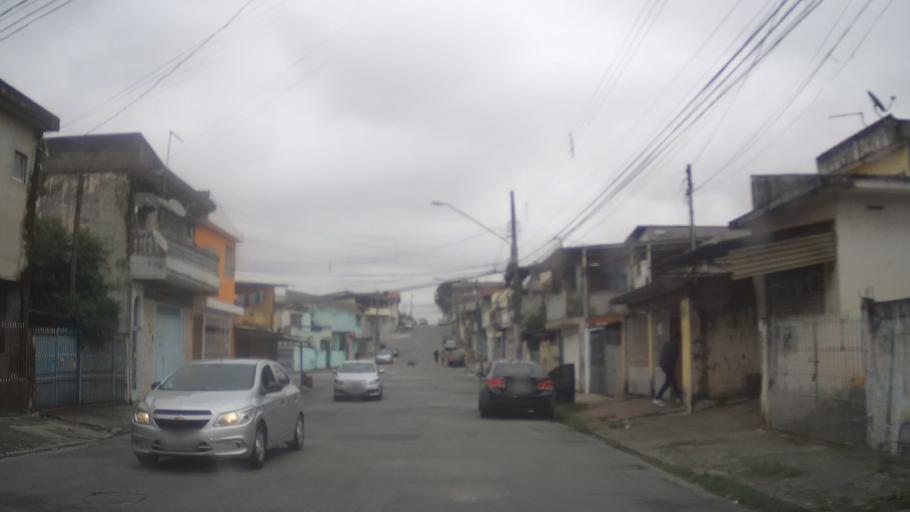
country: BR
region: Sao Paulo
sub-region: Guarulhos
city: Guarulhos
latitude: -23.4357
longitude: -46.5127
